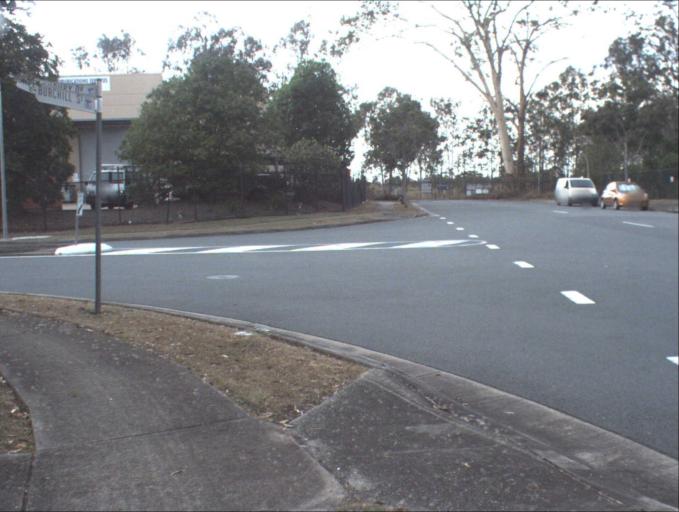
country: AU
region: Queensland
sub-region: Logan
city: Beenleigh
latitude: -27.6862
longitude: 153.1923
